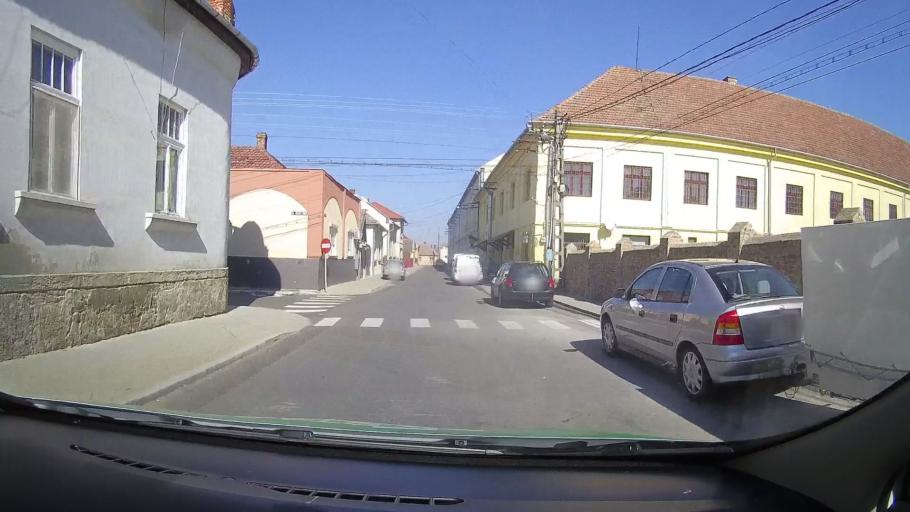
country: RO
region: Satu Mare
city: Carei
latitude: 47.6874
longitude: 22.4666
